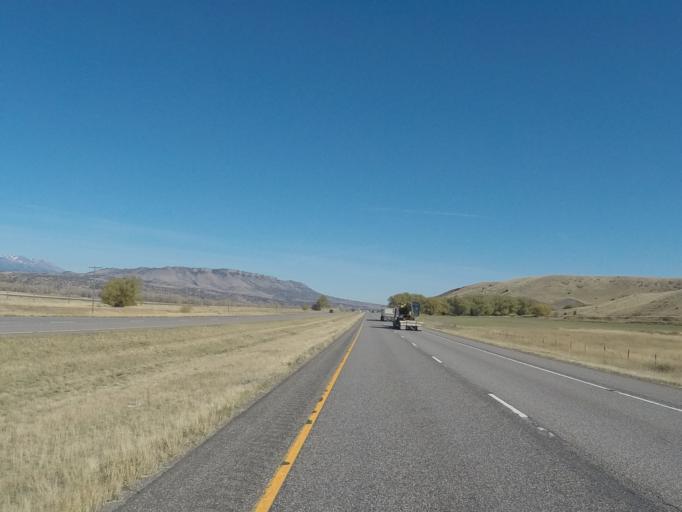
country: US
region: Montana
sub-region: Park County
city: Livingston
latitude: 45.7010
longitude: -110.4692
